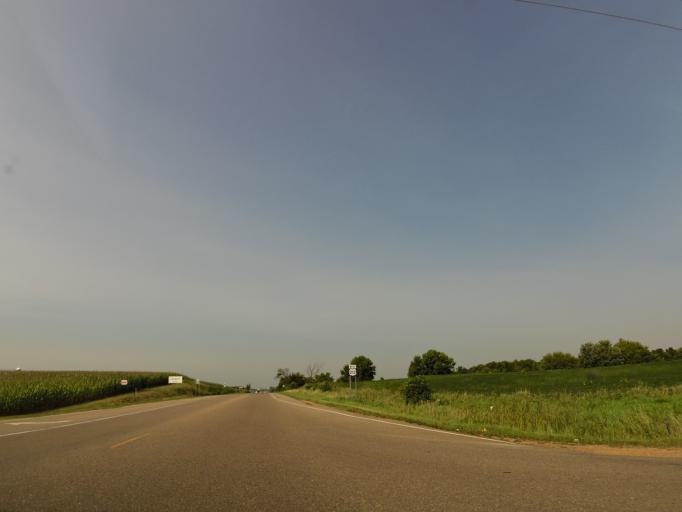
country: US
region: Minnesota
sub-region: Carver County
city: Cologne
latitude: 44.7671
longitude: -93.8281
